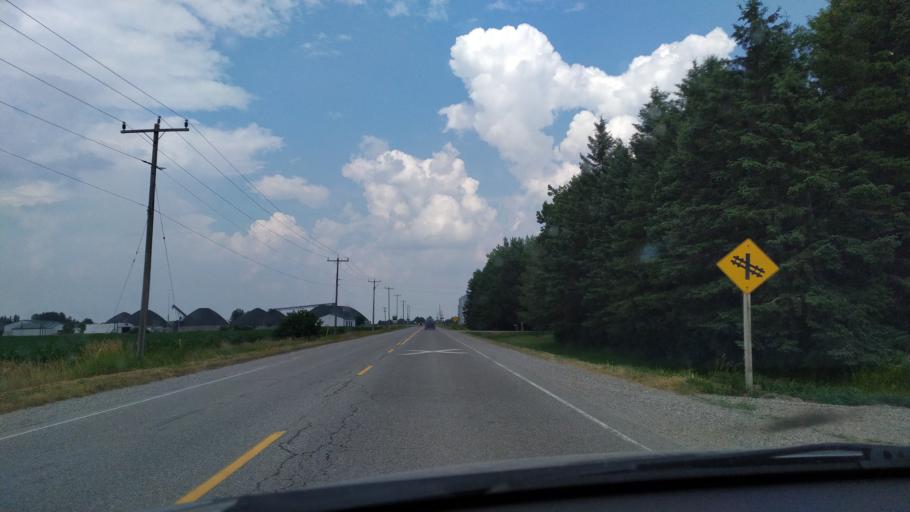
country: CA
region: Ontario
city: Dorchester
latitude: 43.1649
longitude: -81.1437
